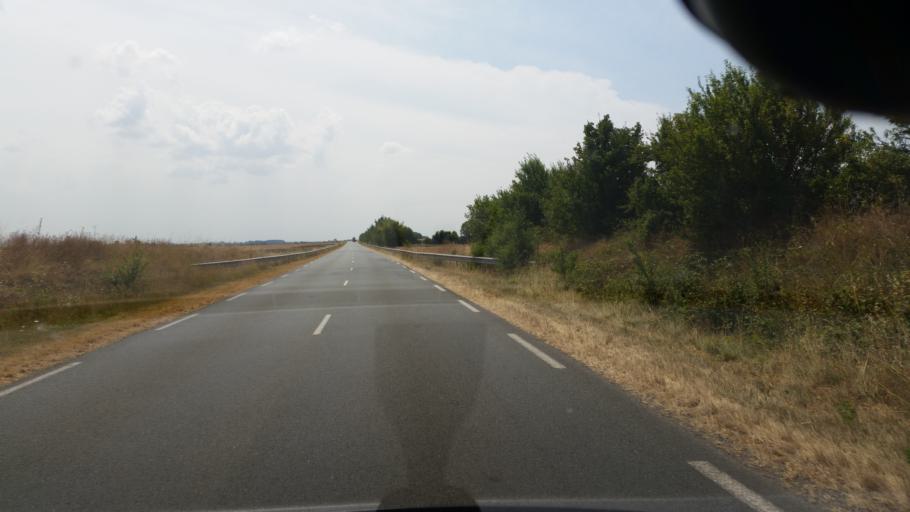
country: FR
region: Poitou-Charentes
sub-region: Departement de la Charente-Maritime
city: Saint-Jean-de-Liversay
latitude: 46.2079
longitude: -0.8749
